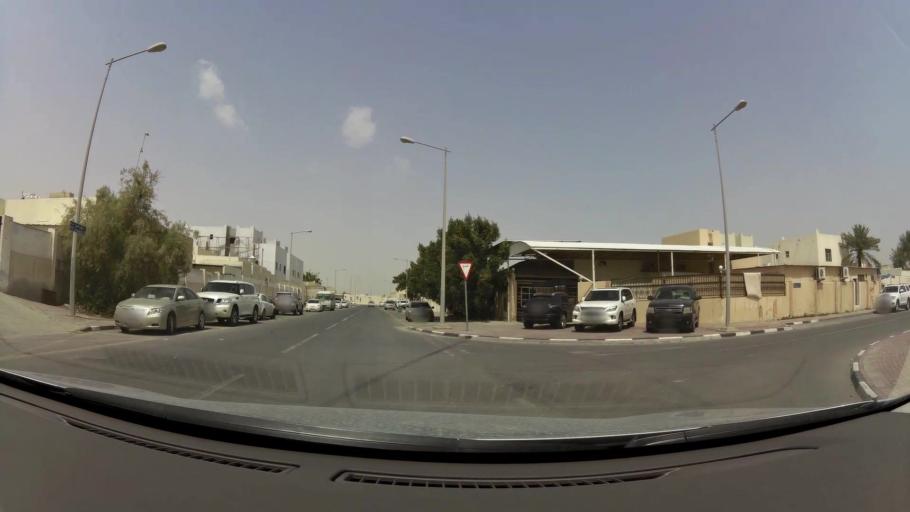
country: QA
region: Baladiyat ar Rayyan
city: Ar Rayyan
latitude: 25.2432
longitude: 51.4262
